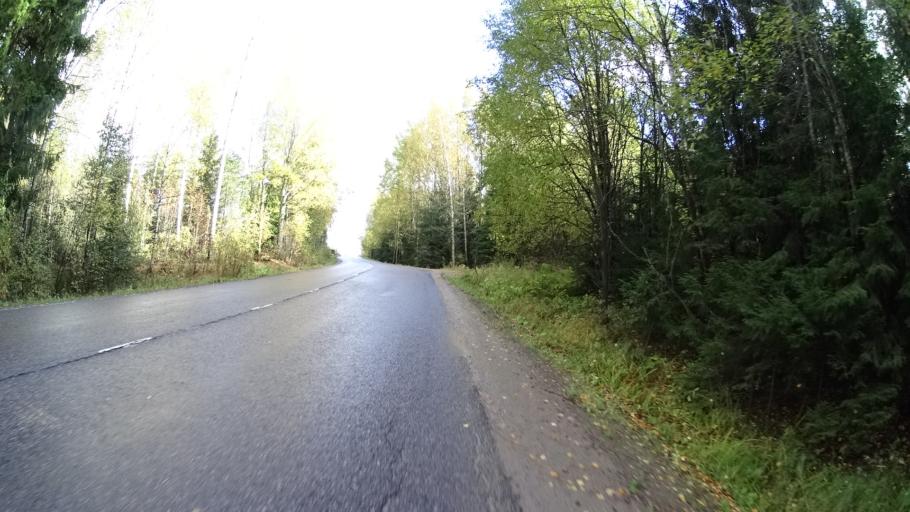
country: FI
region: Uusimaa
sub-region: Helsinki
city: Kilo
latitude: 60.2876
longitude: 24.8091
